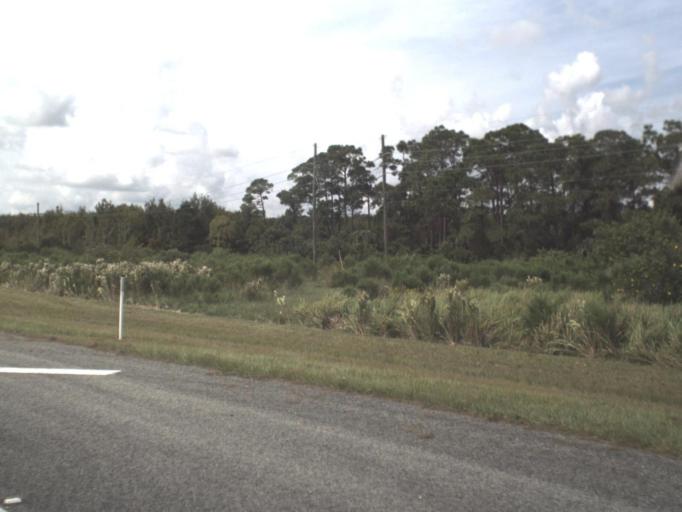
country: US
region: Florida
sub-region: Okeechobee County
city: Taylor Creek
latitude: 27.2932
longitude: -80.6940
